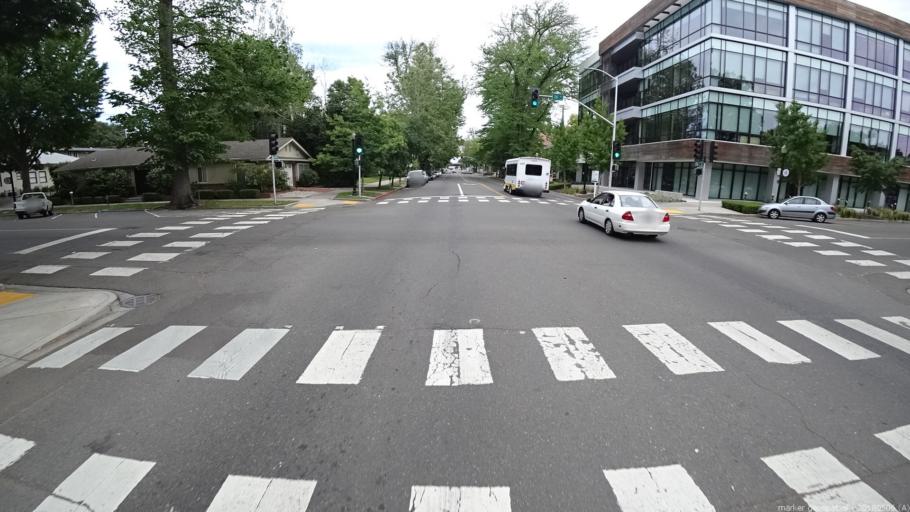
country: US
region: California
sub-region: Sacramento County
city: Sacramento
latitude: 38.5713
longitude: -121.4734
